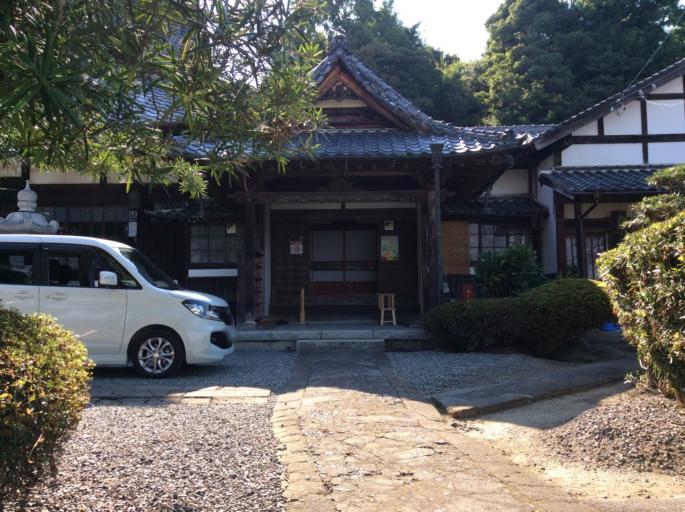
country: JP
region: Shizuoka
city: Fujinomiya
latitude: 35.1053
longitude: 138.5546
